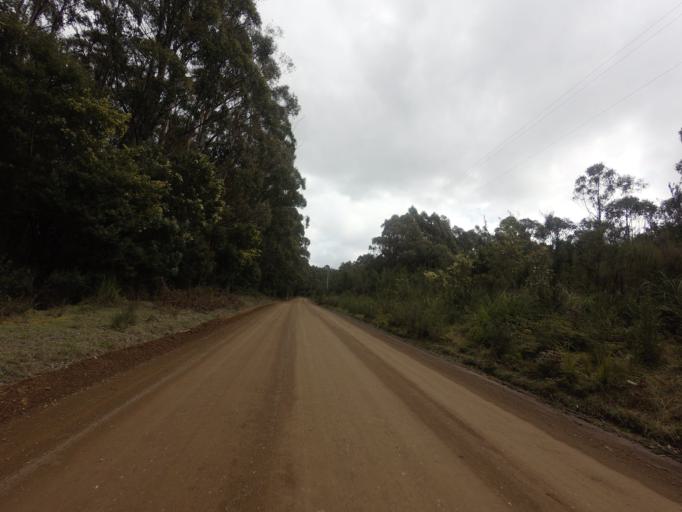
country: AU
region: Tasmania
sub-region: Huon Valley
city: Geeveston
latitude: -43.4142
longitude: 146.9057
